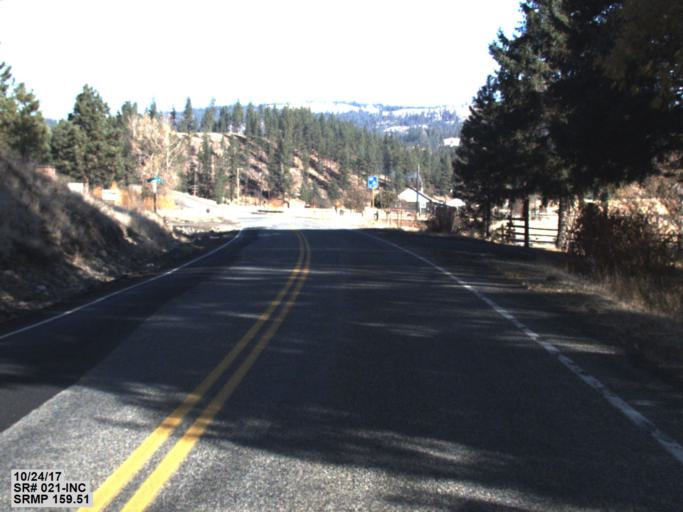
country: US
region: Washington
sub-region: Ferry County
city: Republic
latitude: 48.6325
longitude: -118.7295
